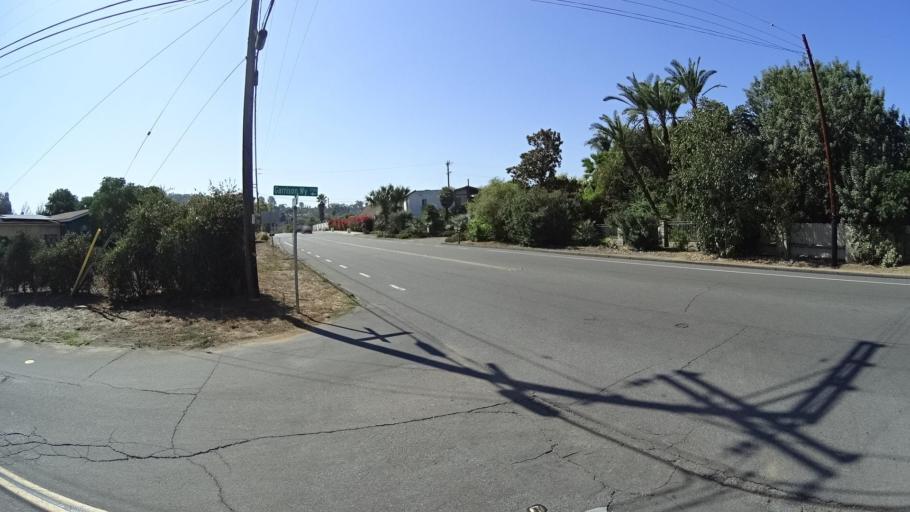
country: US
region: California
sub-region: San Diego County
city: Granite Hills
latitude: 32.7896
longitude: -116.9182
